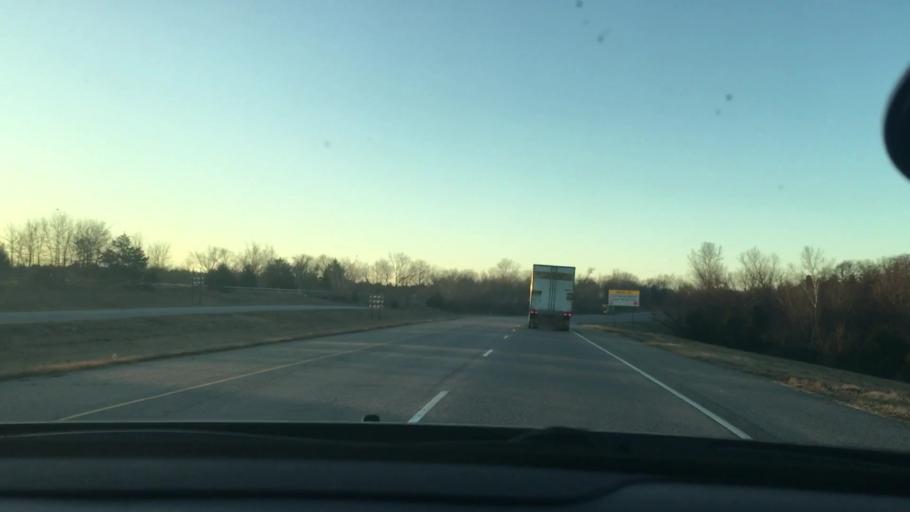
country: US
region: Oklahoma
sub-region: Pontotoc County
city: Ada
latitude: 34.7330
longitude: -96.7090
